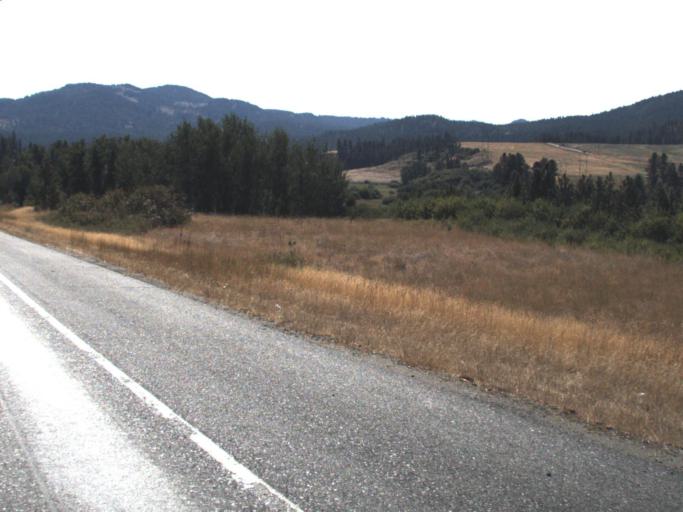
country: US
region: Washington
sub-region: Stevens County
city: Chewelah
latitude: 48.3377
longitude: -117.8301
